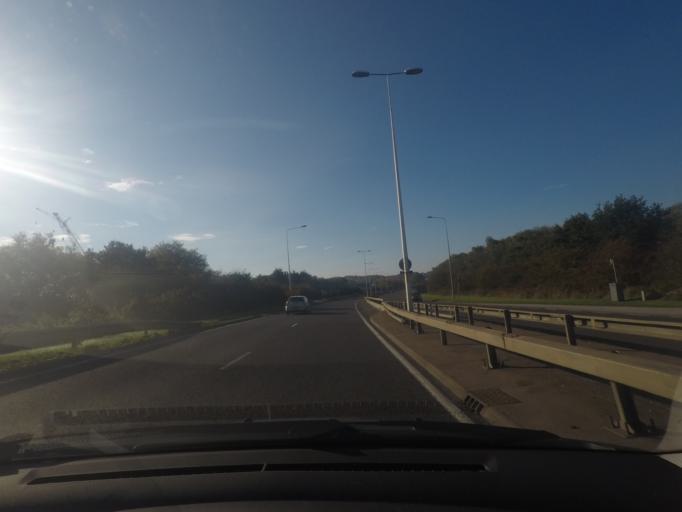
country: GB
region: England
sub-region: North Lincolnshire
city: Barton upon Humber
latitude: 53.6923
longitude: -0.4500
